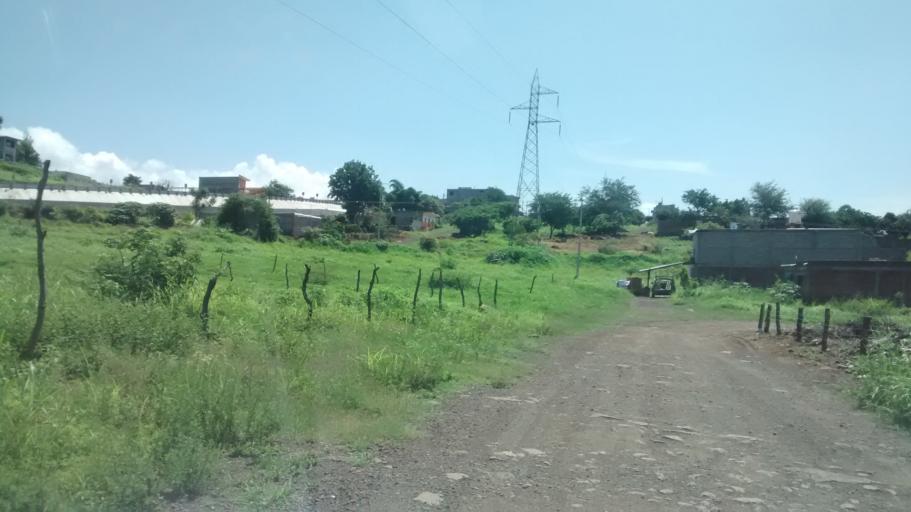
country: MX
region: Nayarit
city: Ixtlan del Rio
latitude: 21.0289
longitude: -104.3563
